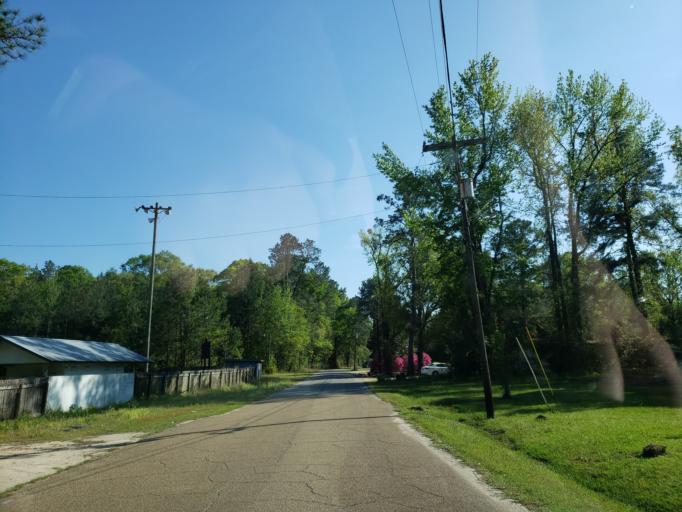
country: US
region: Mississippi
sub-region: Perry County
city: New Augusta
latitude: 31.1645
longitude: -88.9209
